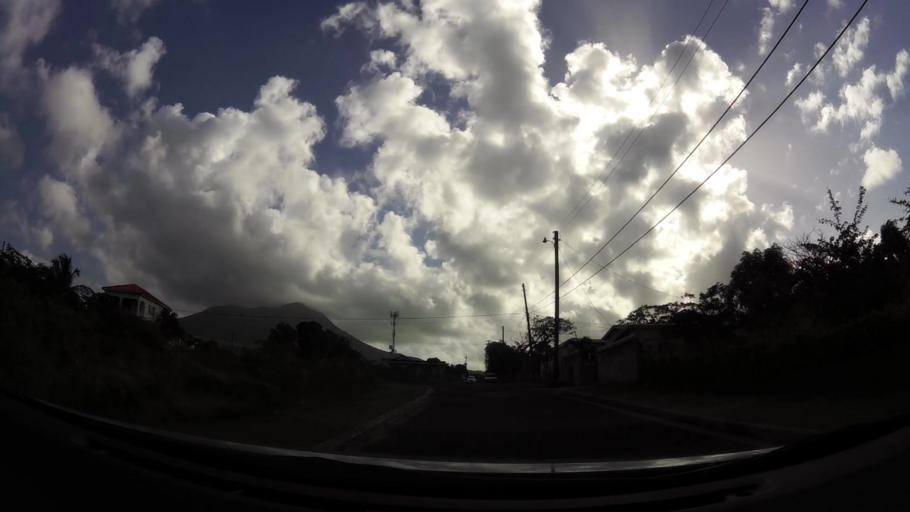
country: KN
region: Saint Paul Charlestown
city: Charlestown
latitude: 17.1386
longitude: -62.6241
